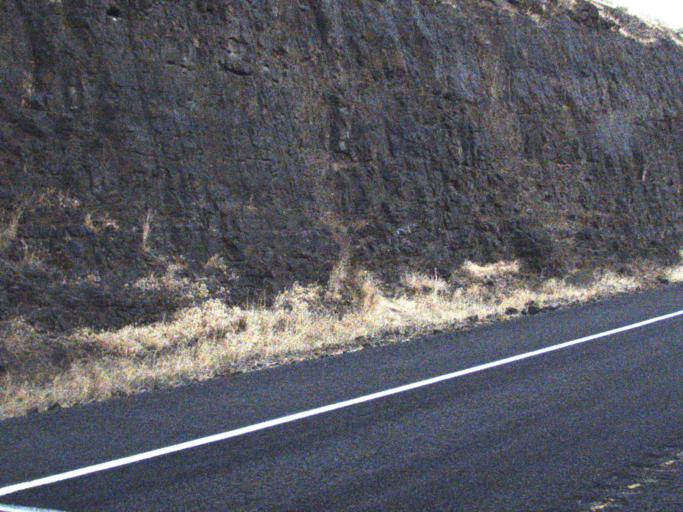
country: US
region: Washington
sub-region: Adams County
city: Ritzville
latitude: 46.7540
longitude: -118.1843
